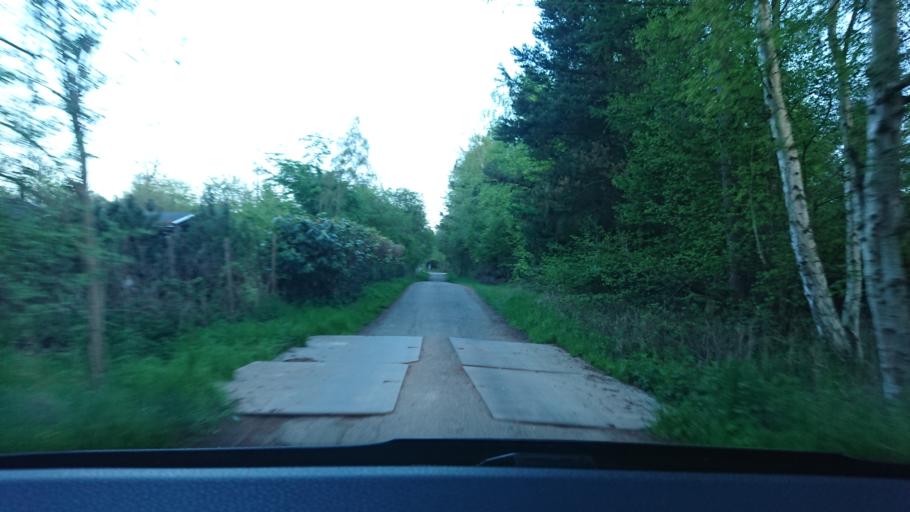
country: DK
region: Zealand
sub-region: Odsherred Kommune
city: Nykobing Sjaelland
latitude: 55.9394
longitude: 11.6971
